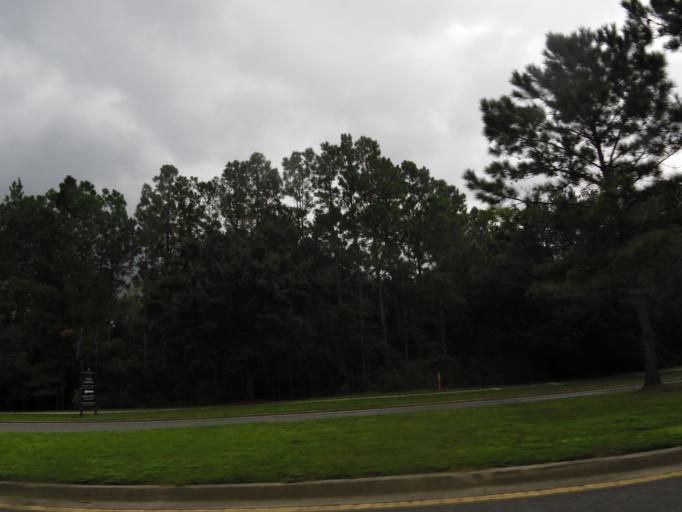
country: US
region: Florida
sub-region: Clay County
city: Lakeside
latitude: 30.1664
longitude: -81.8475
